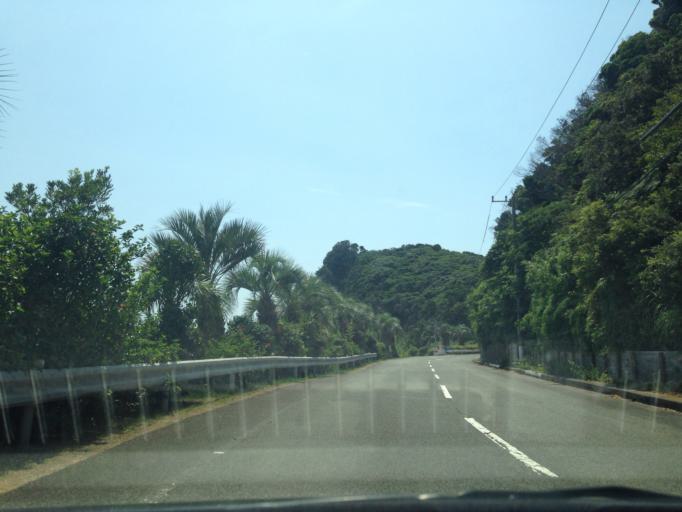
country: JP
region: Shizuoka
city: Shimoda
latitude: 34.6205
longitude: 138.8739
